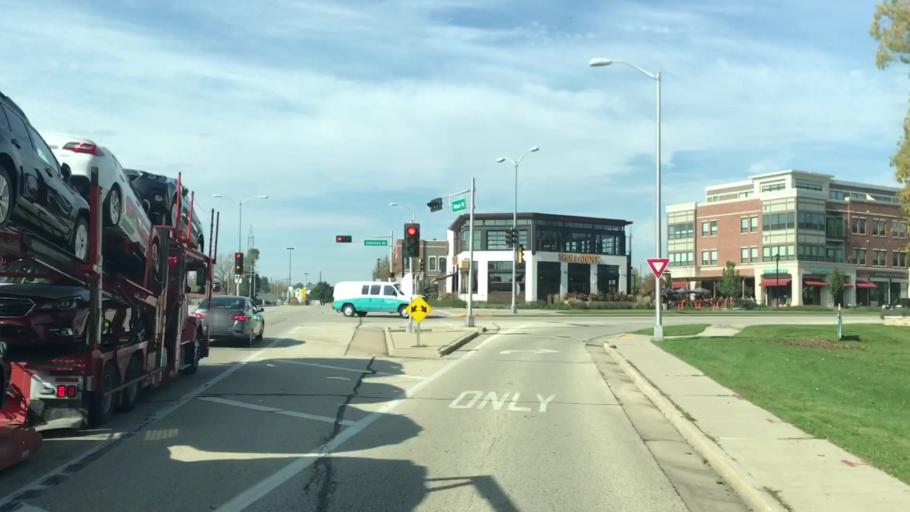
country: US
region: Wisconsin
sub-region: Ozaukee County
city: Mequon
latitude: 43.2217
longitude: -87.9821
